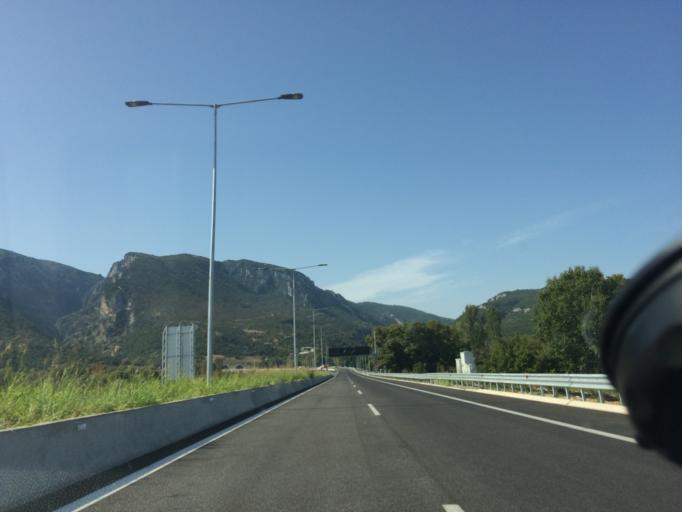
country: GR
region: Thessaly
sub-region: Nomos Larisis
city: Pyrgetos
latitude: 39.8991
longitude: 22.6180
